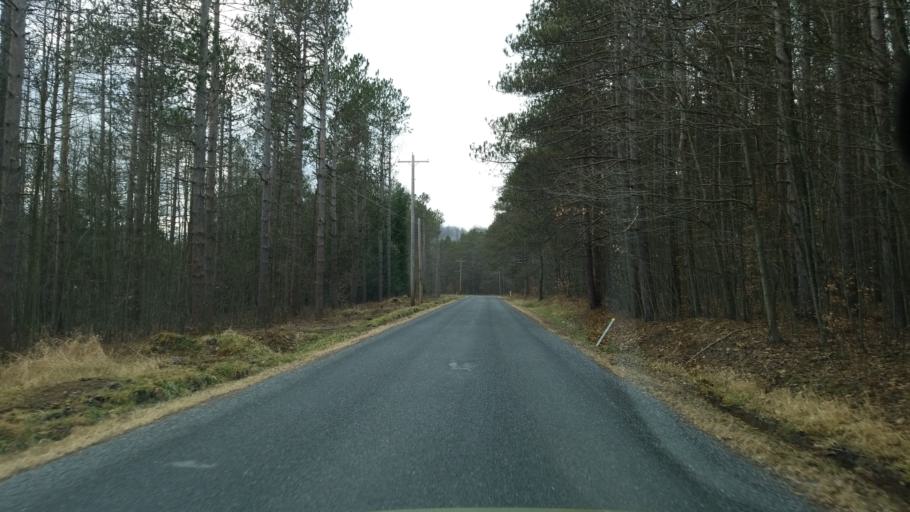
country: US
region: Pennsylvania
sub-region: Clearfield County
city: Treasure Lake
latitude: 41.1481
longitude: -78.5732
